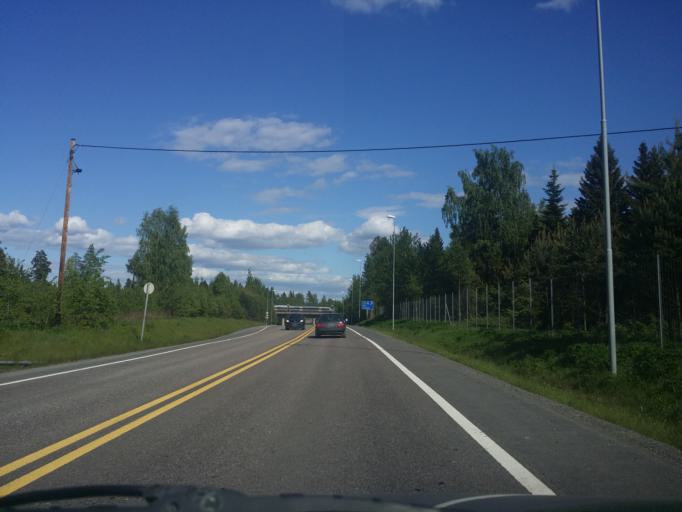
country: NO
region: Akershus
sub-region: Nannestad
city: Teigebyen
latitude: 60.1780
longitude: 11.0872
